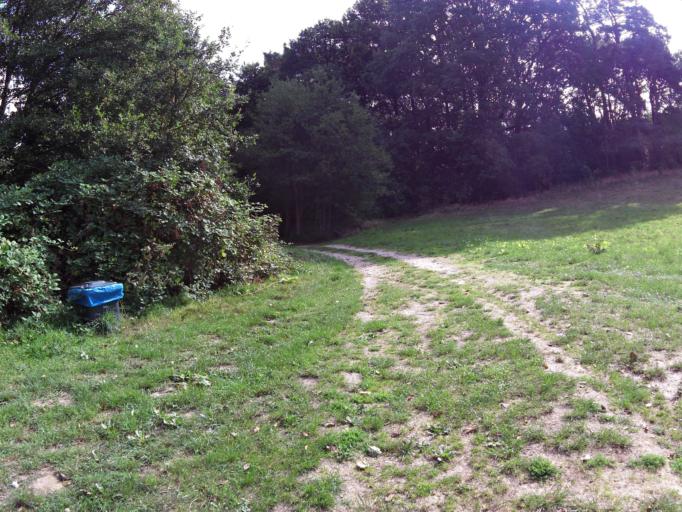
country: DE
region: Mecklenburg-Vorpommern
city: Seebad Bansin
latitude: 53.9504
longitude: 14.1098
